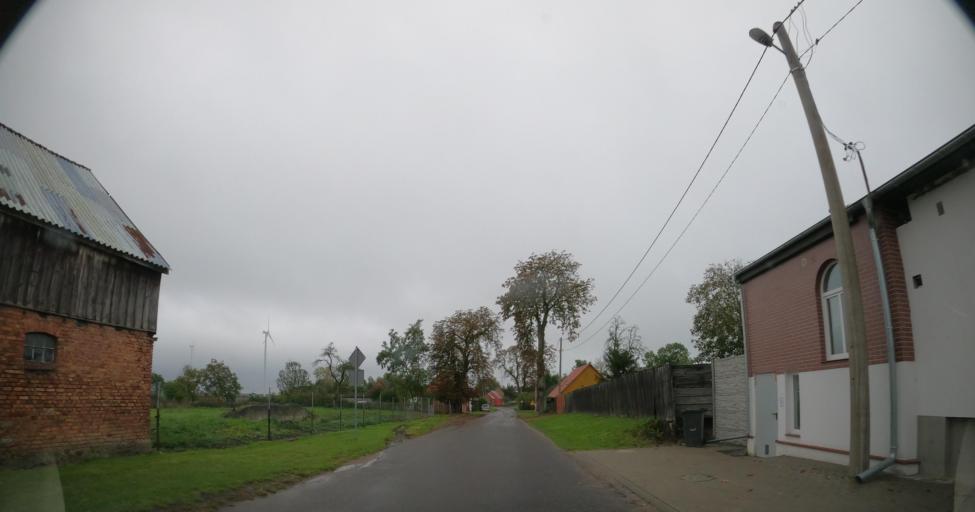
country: PL
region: West Pomeranian Voivodeship
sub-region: Powiat pyrzycki
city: Kozielice
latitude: 53.0920
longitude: 14.7712
